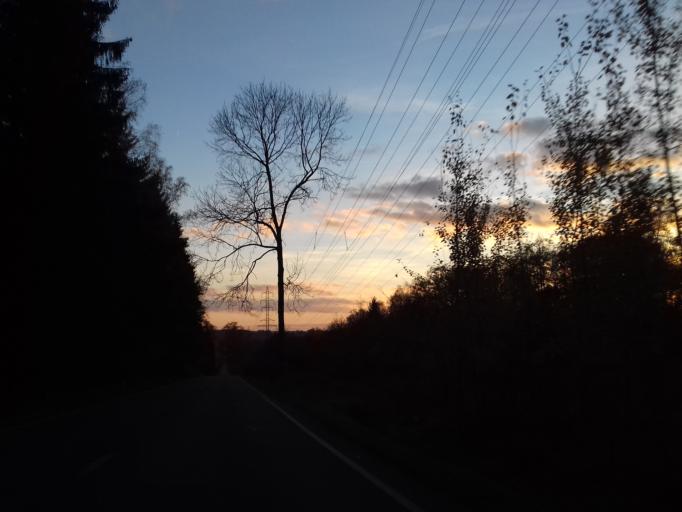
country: CZ
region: Pardubicky
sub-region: Okres Chrudim
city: Hlinsko
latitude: 49.7352
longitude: 15.8757
